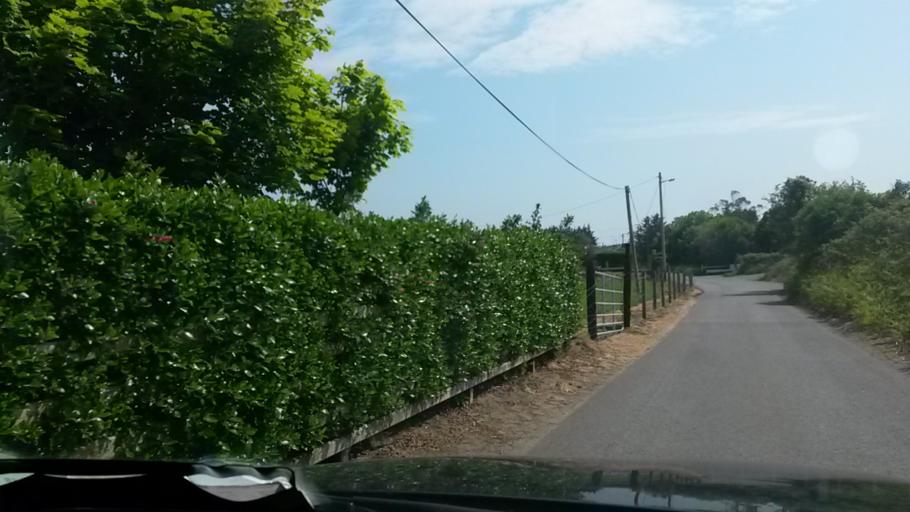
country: IE
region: Leinster
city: Portraine
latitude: 53.5037
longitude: -6.1228
